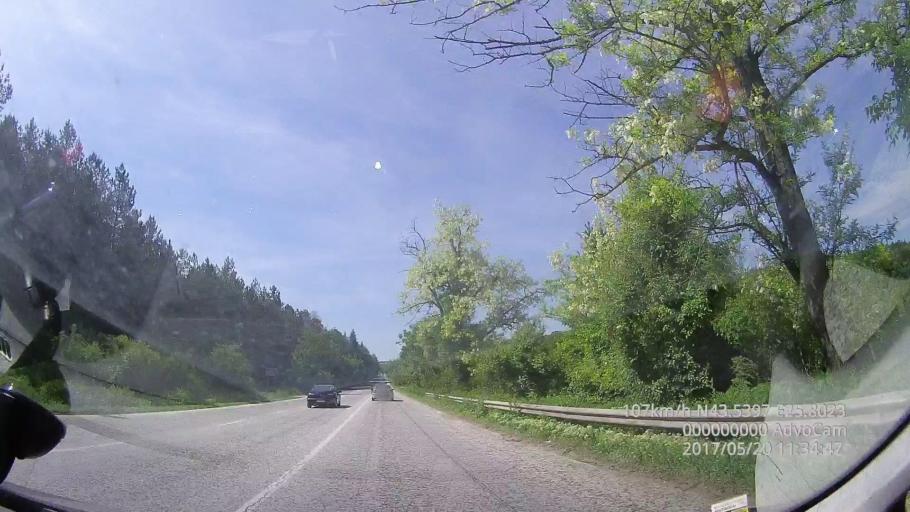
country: BG
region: Ruse
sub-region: Obshtina Borovo
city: Borovo
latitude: 43.5390
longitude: 25.8021
